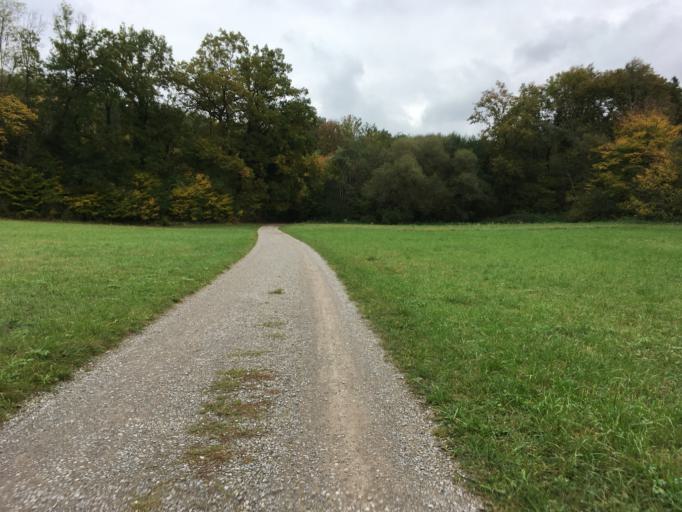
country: DE
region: Baden-Wuerttemberg
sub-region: Tuebingen Region
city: Gomaringen
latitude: 48.4807
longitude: 9.0792
